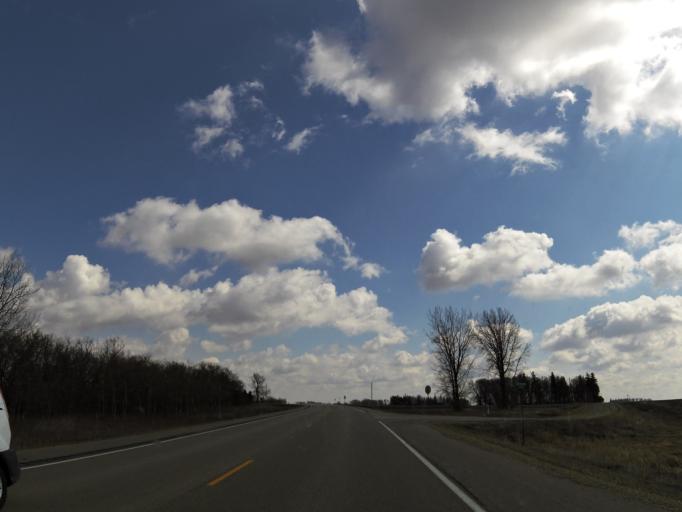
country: US
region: Minnesota
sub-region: Goodhue County
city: Kenyon
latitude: 44.2422
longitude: -92.9605
